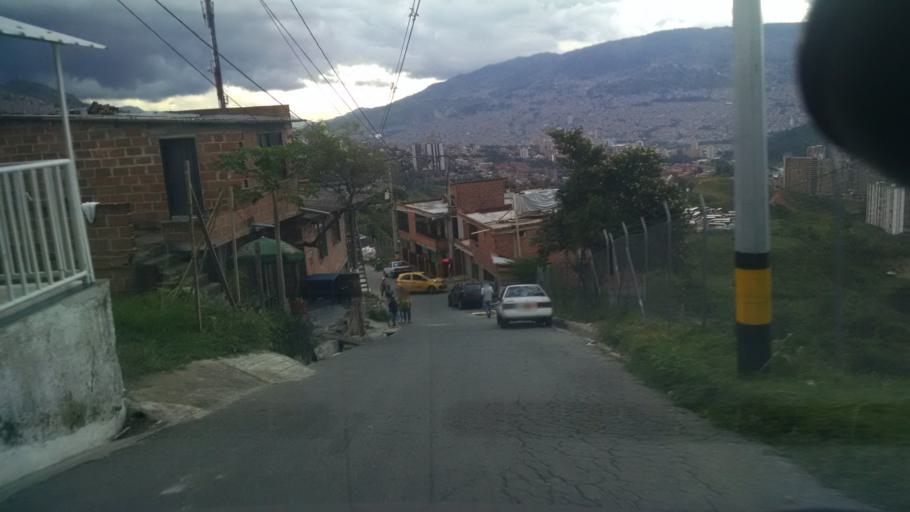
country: CO
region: Antioquia
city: Medellin
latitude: 6.2716
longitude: -75.6123
